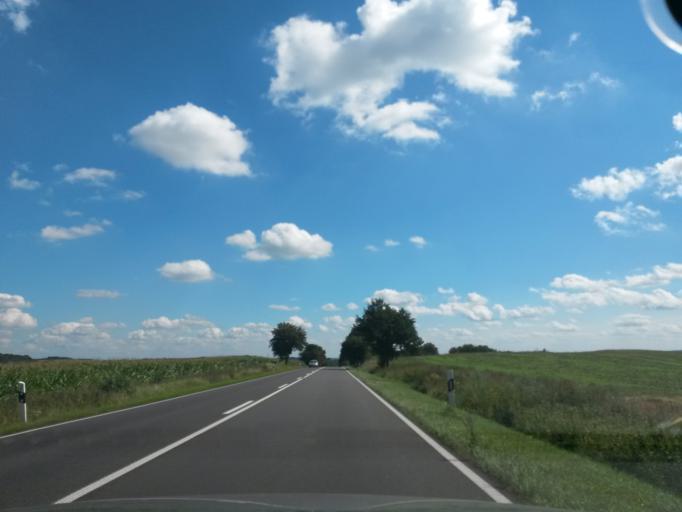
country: DE
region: Brandenburg
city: Schoneberg
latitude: 53.0326
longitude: 14.1452
